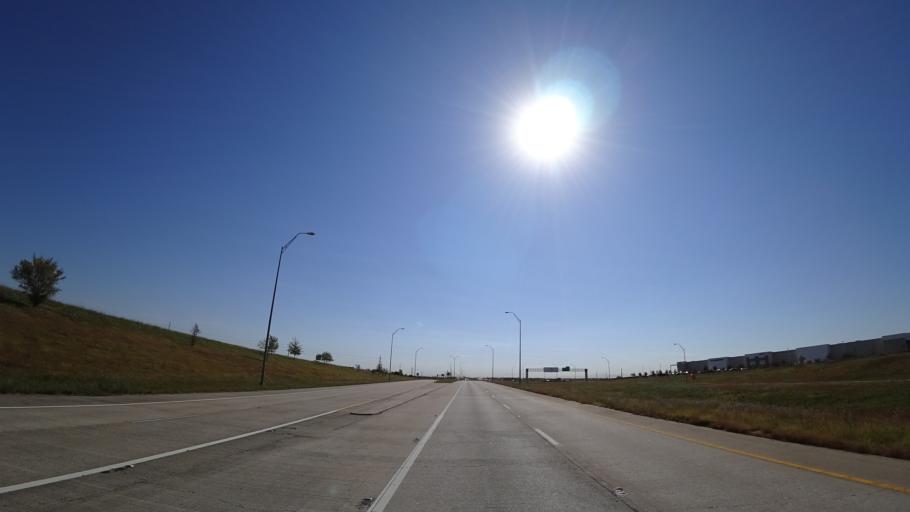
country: US
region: Texas
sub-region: Travis County
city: Pflugerville
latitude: 30.4219
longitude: -97.5872
